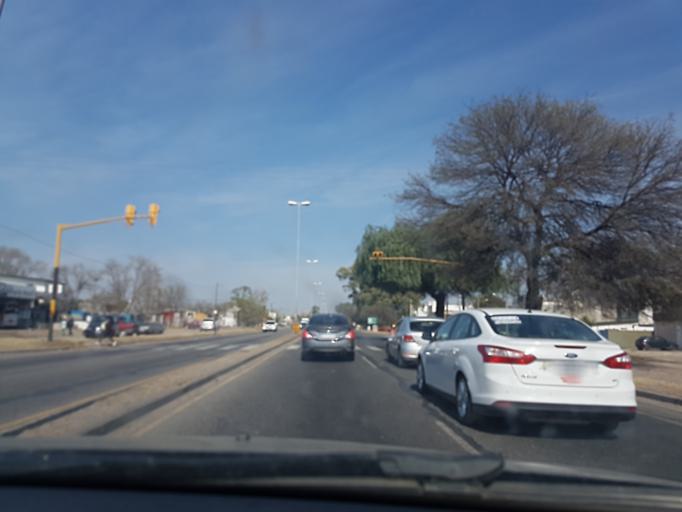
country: AR
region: Cordoba
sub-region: Departamento de Capital
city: Cordoba
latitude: -31.4715
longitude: -64.2297
